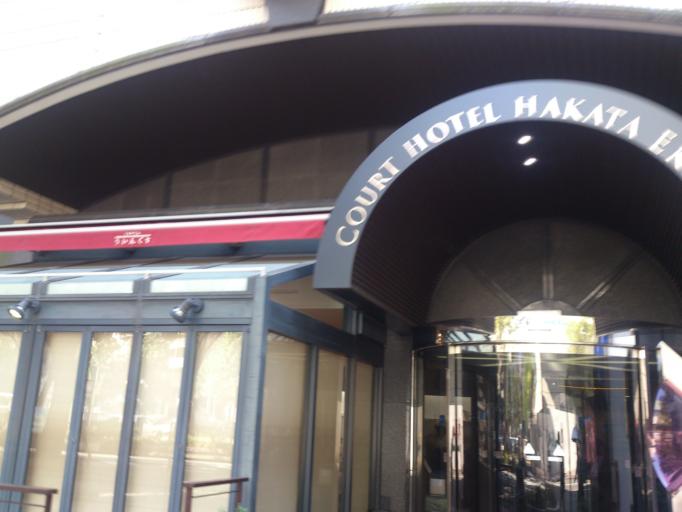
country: JP
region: Fukuoka
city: Fukuoka-shi
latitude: 33.5902
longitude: 130.4134
